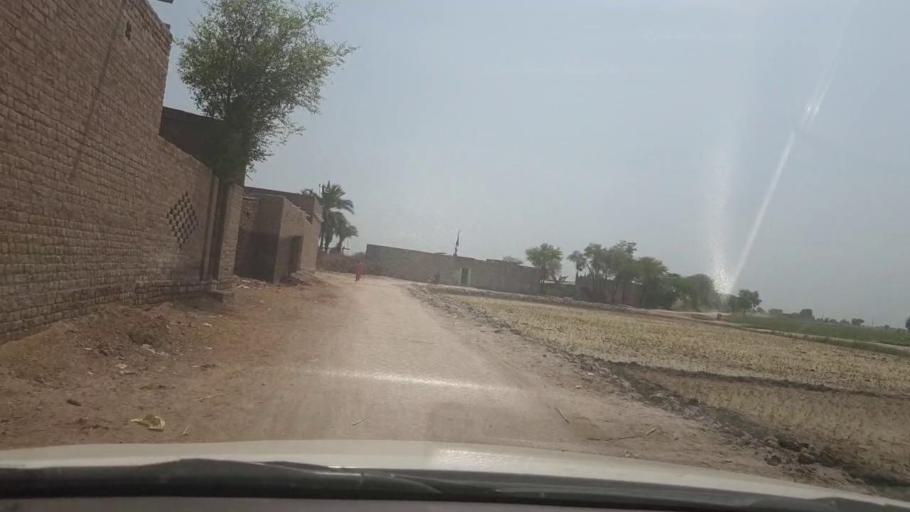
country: PK
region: Sindh
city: Shikarpur
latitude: 27.9973
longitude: 68.5886
